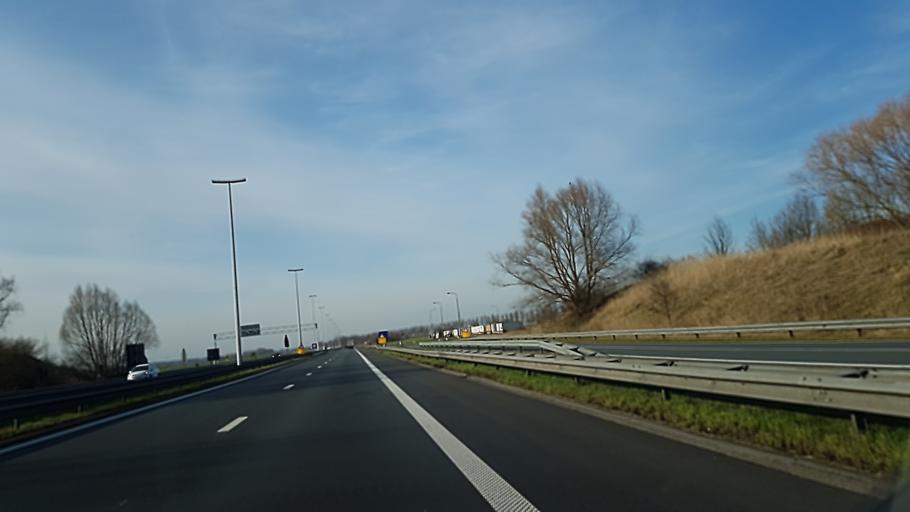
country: NL
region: North Brabant
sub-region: Gemeente Woensdrecht
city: Woensdrecht
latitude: 51.3756
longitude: 4.3052
